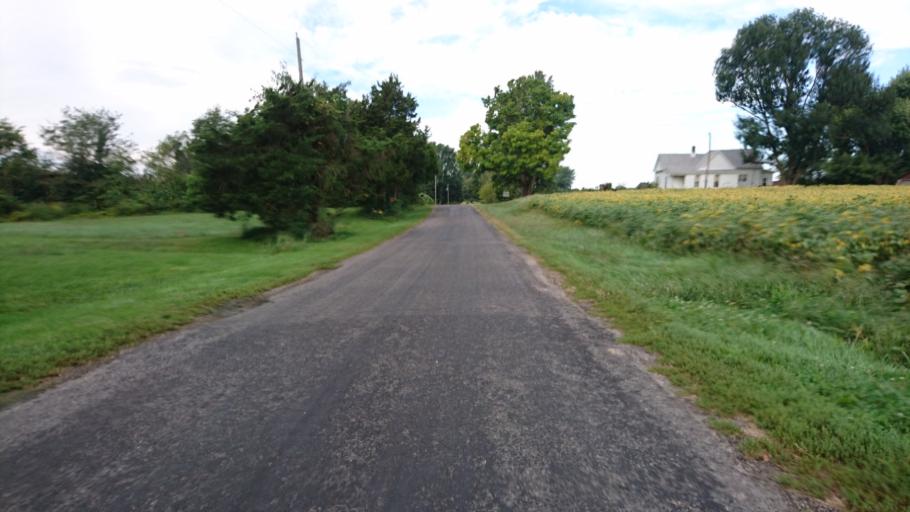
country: US
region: Illinois
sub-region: Macoupin County
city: Staunton
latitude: 38.9903
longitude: -89.7212
